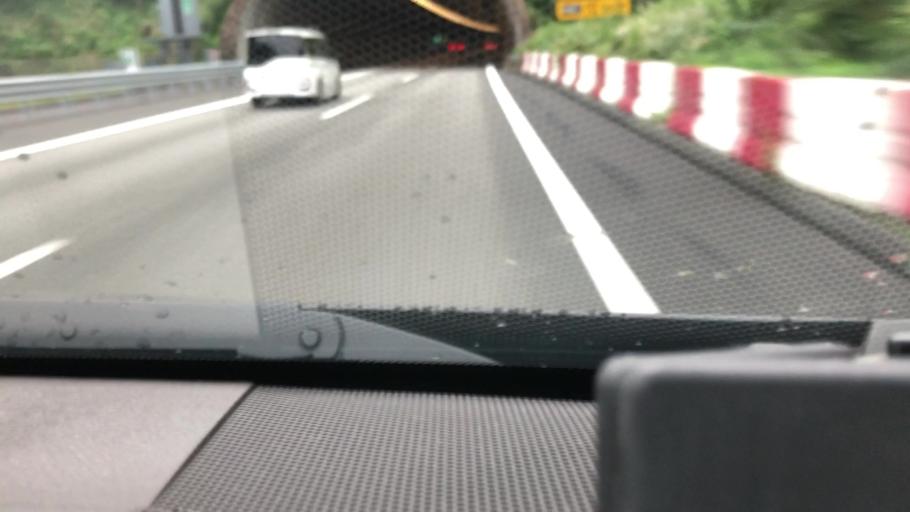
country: JP
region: Shizuoka
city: Mori
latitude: 34.8444
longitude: 138.0084
